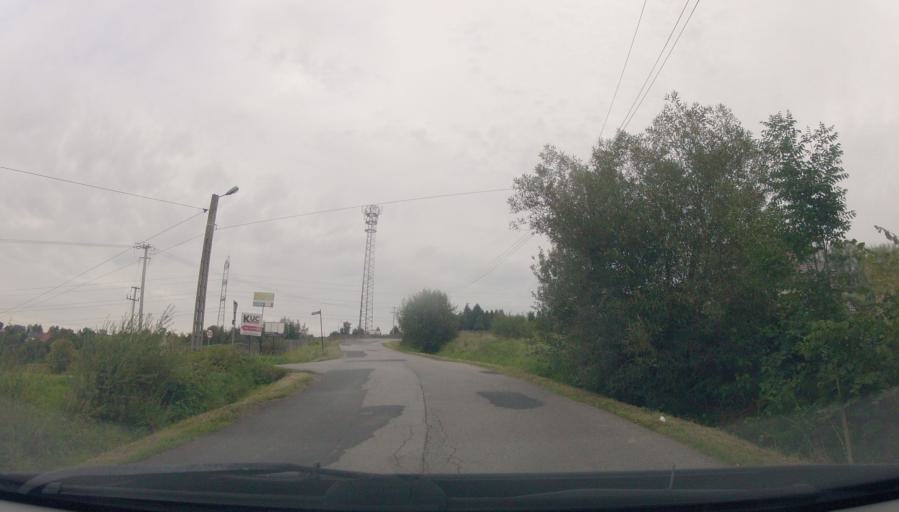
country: PL
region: Lesser Poland Voivodeship
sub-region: Powiat krakowski
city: Ochojno
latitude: 49.9439
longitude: 19.9955
